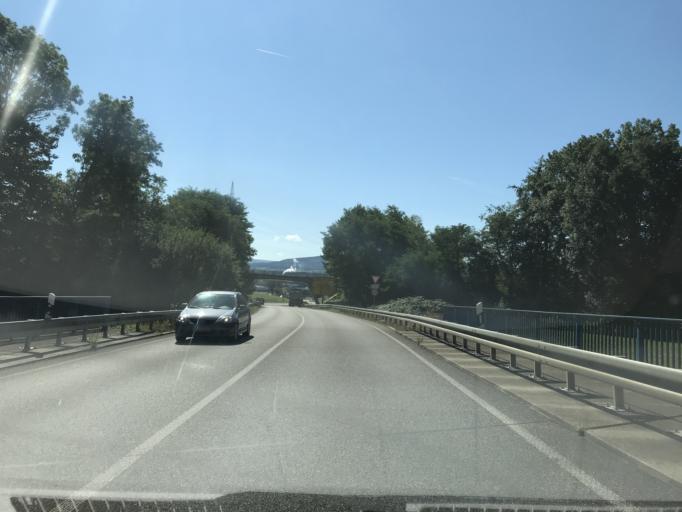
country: DE
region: Baden-Wuerttemberg
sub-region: Freiburg Region
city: Rheinfelden (Baden)
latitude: 47.5787
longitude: 7.7936
